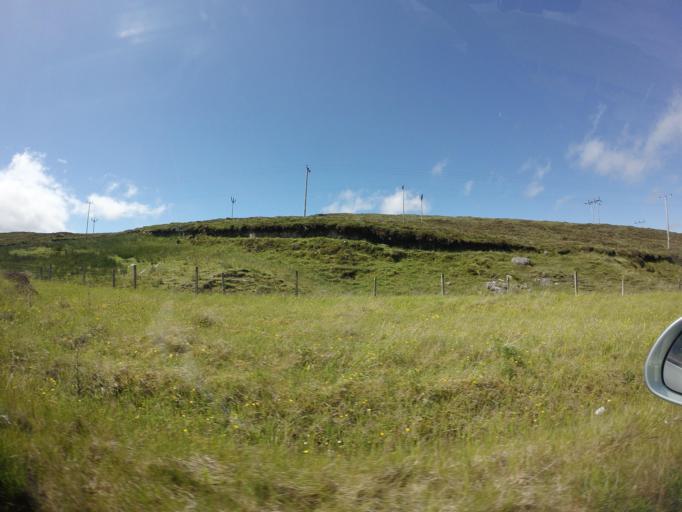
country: GB
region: Scotland
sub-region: Eilean Siar
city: Stornoway
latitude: 58.1289
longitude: -6.5064
